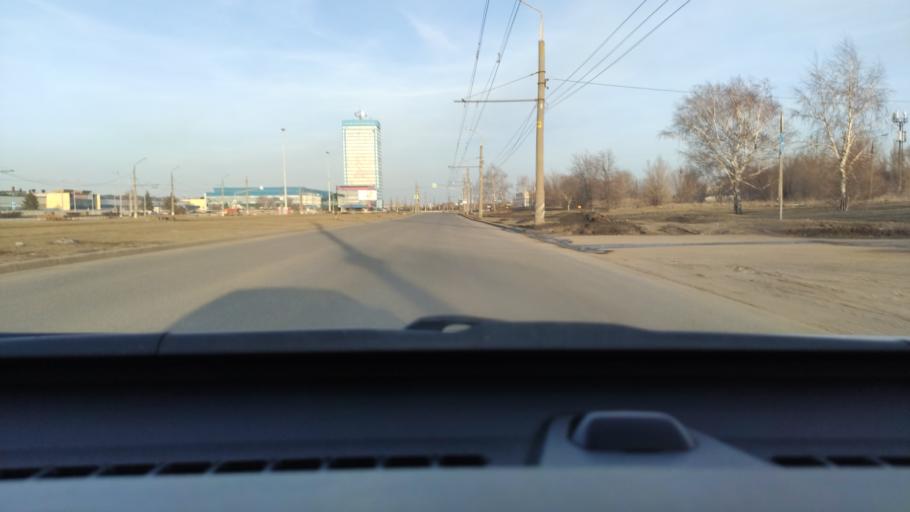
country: RU
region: Samara
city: Tol'yatti
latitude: 53.5580
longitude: 49.2550
